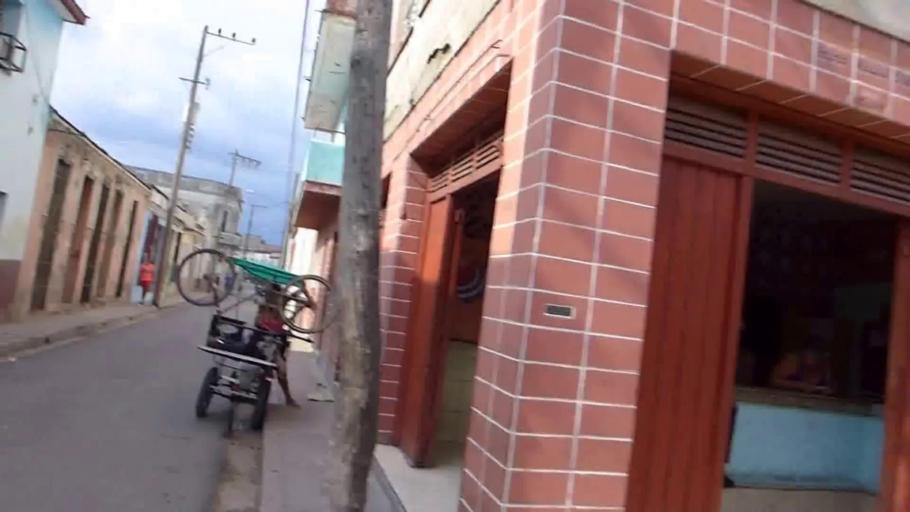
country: CU
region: Camaguey
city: Camaguey
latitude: 21.3849
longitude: -77.9190
